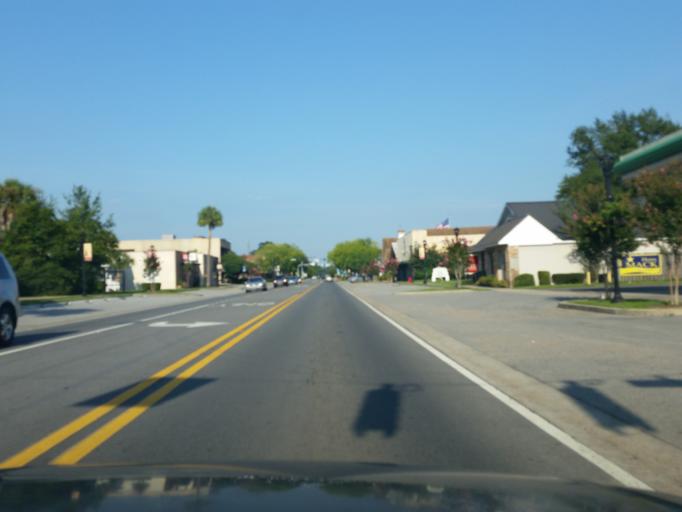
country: US
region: Alabama
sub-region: Baldwin County
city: Foley
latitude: 30.4064
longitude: -87.6870
